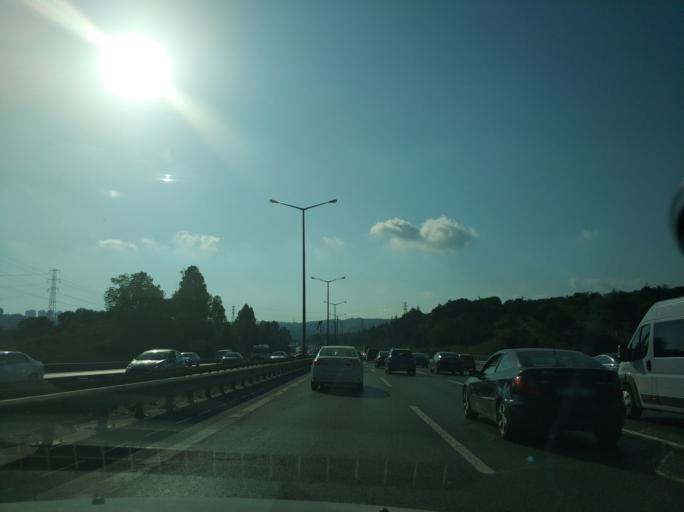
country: TR
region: Istanbul
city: Sisli
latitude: 41.0934
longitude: 28.9332
